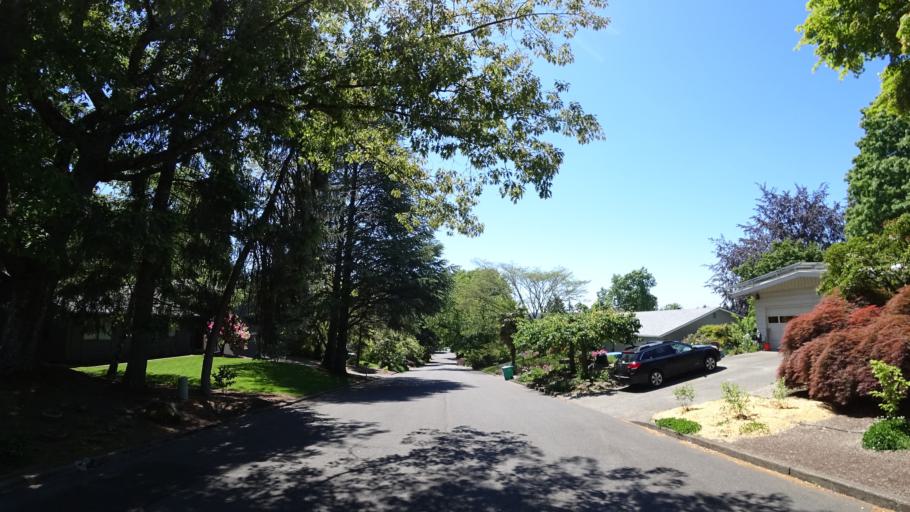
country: US
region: Oregon
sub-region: Washington County
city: Raleigh Hills
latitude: 45.4946
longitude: -122.7212
